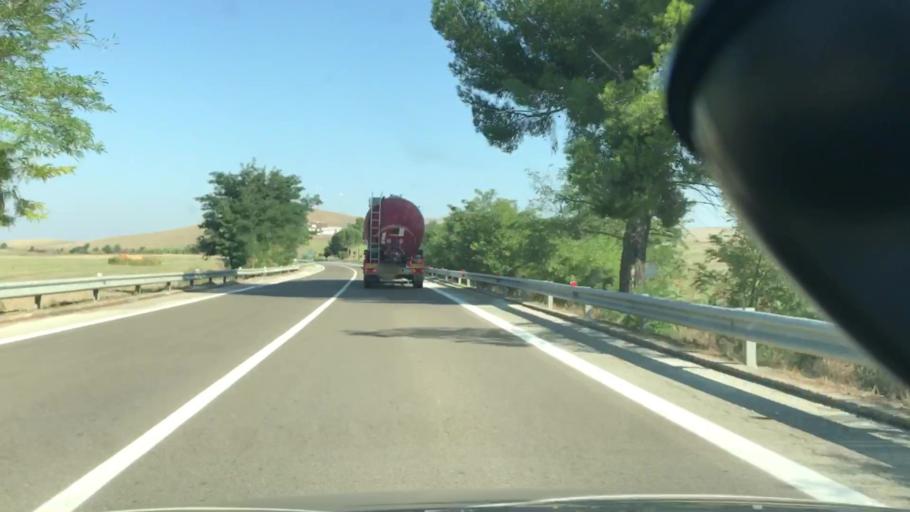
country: IT
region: Basilicate
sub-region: Provincia di Matera
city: Irsina
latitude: 40.8043
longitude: 16.2737
